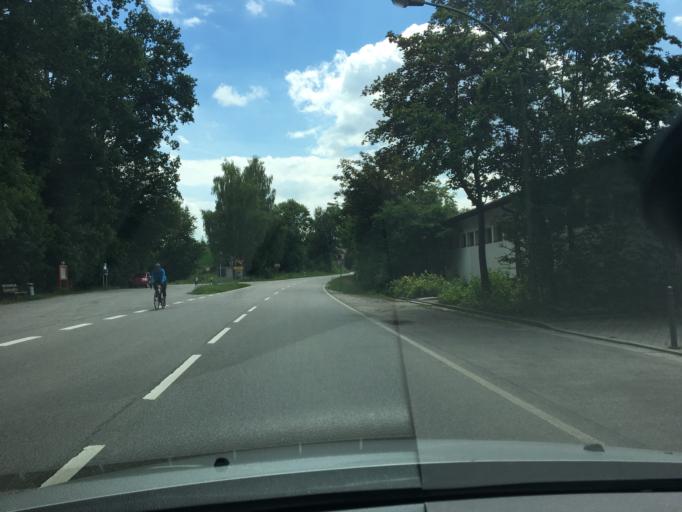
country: DE
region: Bavaria
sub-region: Lower Bavaria
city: Vilsbiburg
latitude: 48.4417
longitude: 12.3529
